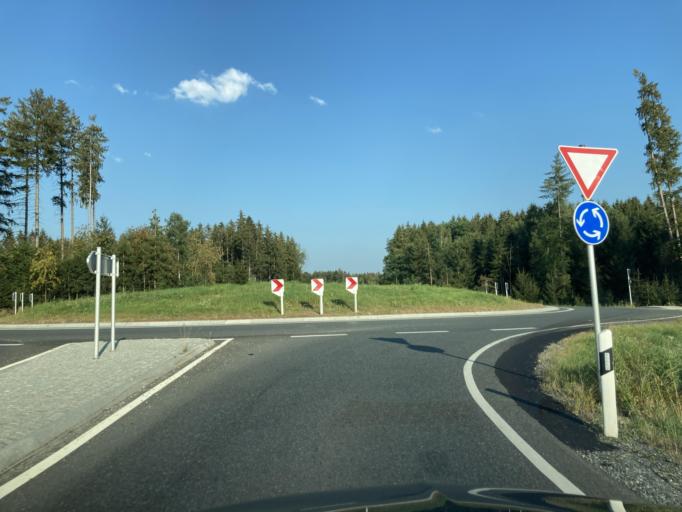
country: DE
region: Bavaria
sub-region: Upper Bavaria
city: Obing
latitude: 48.0120
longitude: 12.4144
